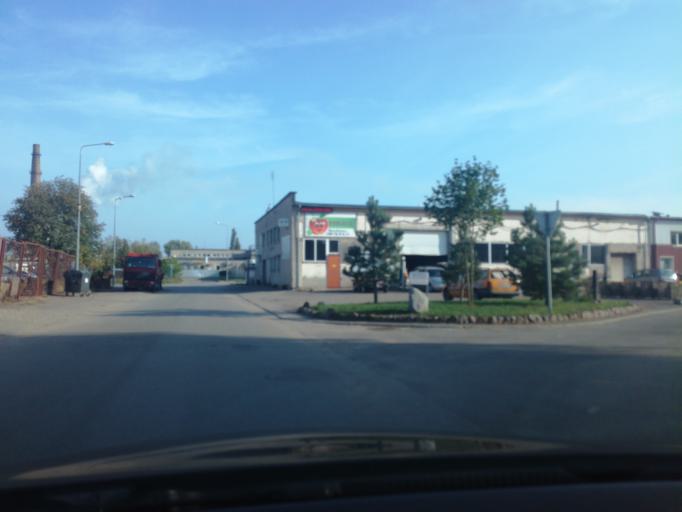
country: LT
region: Alytaus apskritis
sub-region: Alytus
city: Alytus
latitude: 54.4347
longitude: 24.0238
